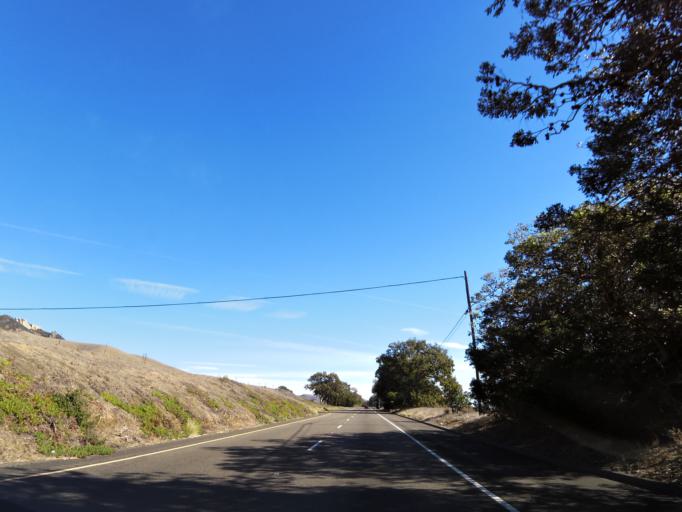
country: US
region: California
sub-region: Santa Barbara County
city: Solvang
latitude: 34.4714
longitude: -120.1777
